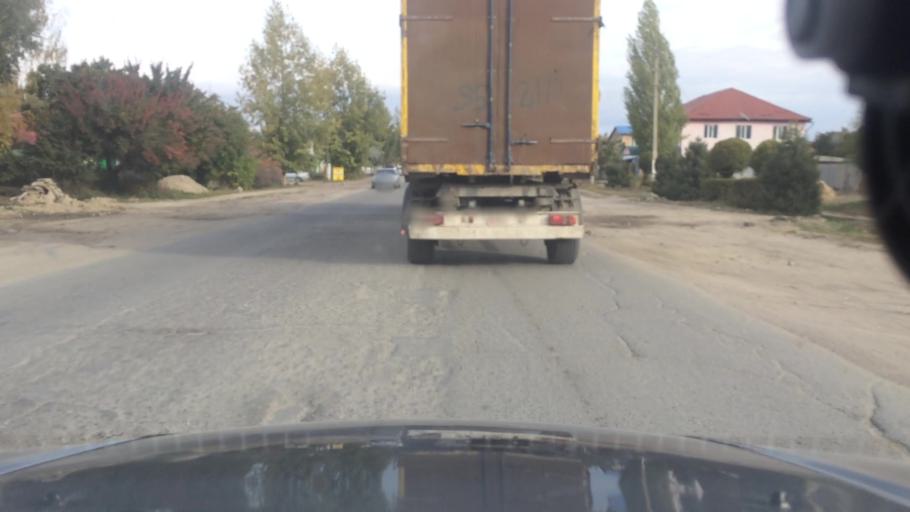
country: KG
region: Ysyk-Koel
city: Karakol
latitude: 42.5187
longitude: 78.3858
